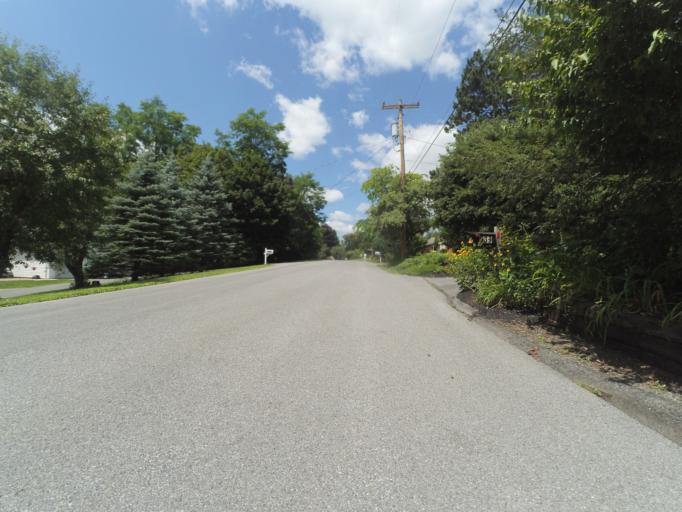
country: US
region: Pennsylvania
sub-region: Centre County
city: Boalsburg
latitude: 40.7831
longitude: -77.8043
